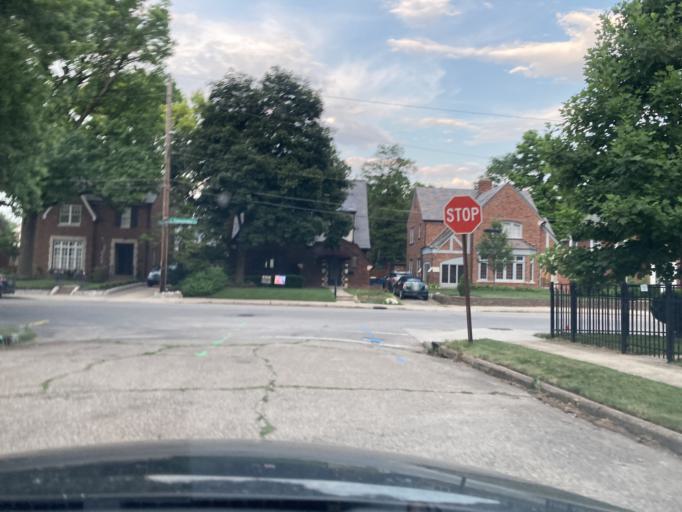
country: US
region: Indiana
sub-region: Marion County
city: Broad Ripple
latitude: 39.8387
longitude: -86.1550
